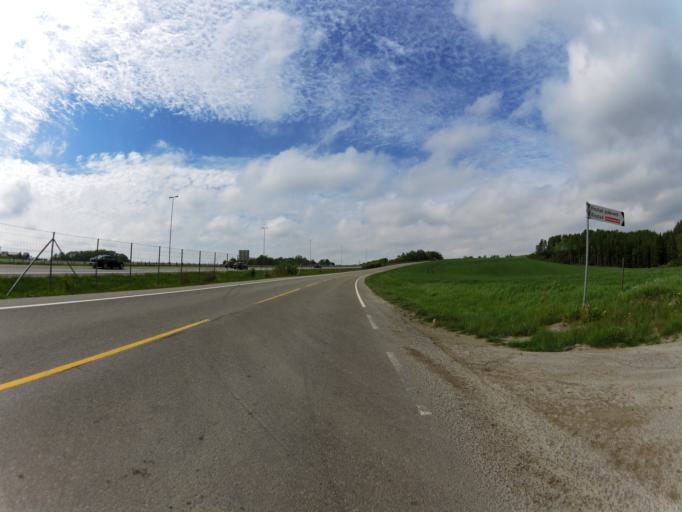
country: NO
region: Ostfold
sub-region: Rade
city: Karlshus
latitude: 59.3252
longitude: 10.9450
